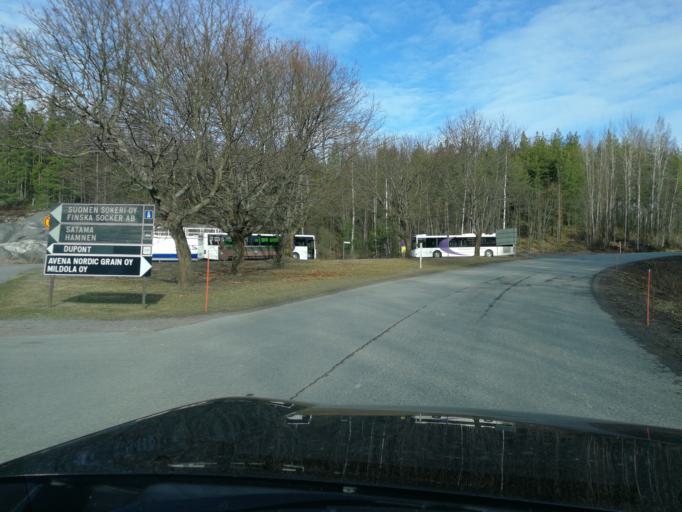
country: FI
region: Uusimaa
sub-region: Helsinki
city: Kirkkonummi
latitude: 60.0905
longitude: 24.3821
